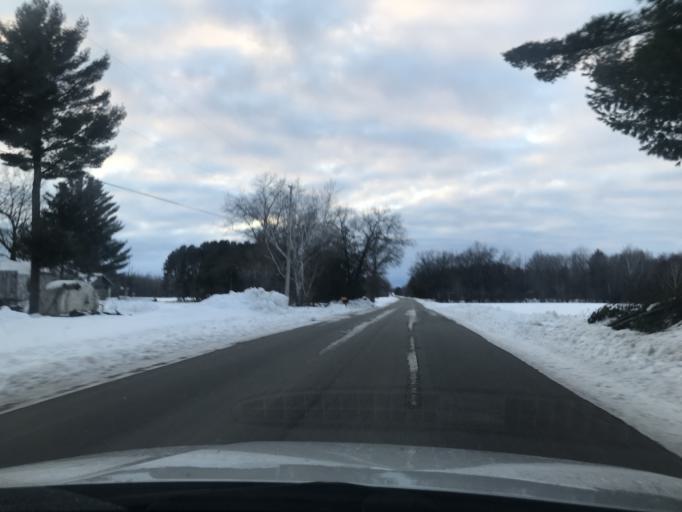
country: US
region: Wisconsin
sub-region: Marinette County
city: Peshtigo
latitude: 45.1645
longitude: -87.7355
